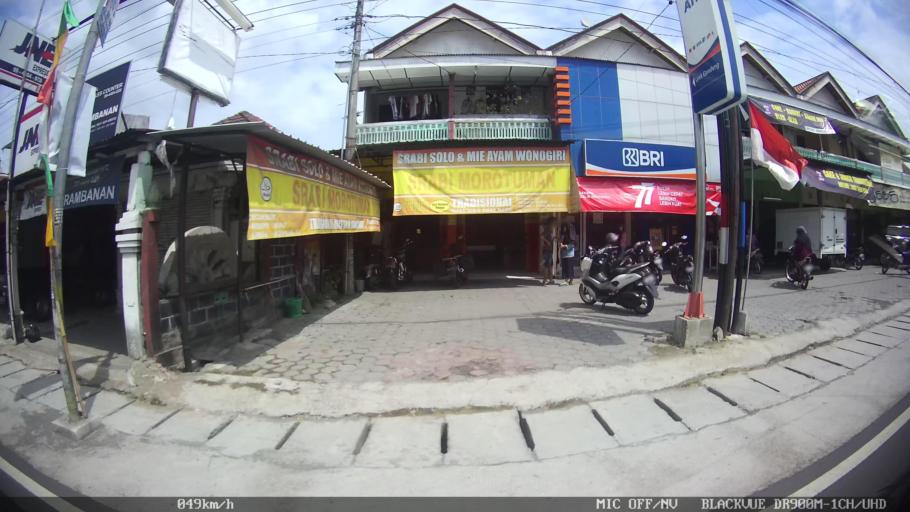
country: ID
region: Central Java
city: Candi Prambanan
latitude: -7.7942
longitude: 110.4828
